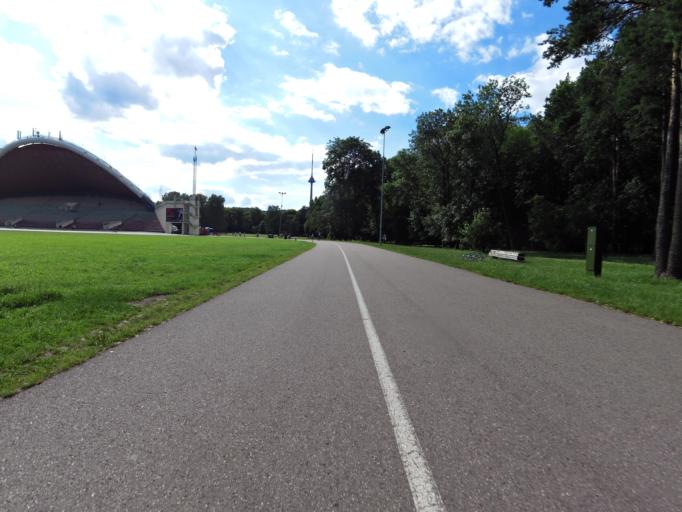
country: LT
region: Vilnius County
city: Vilkpede
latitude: 54.6837
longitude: 25.2384
